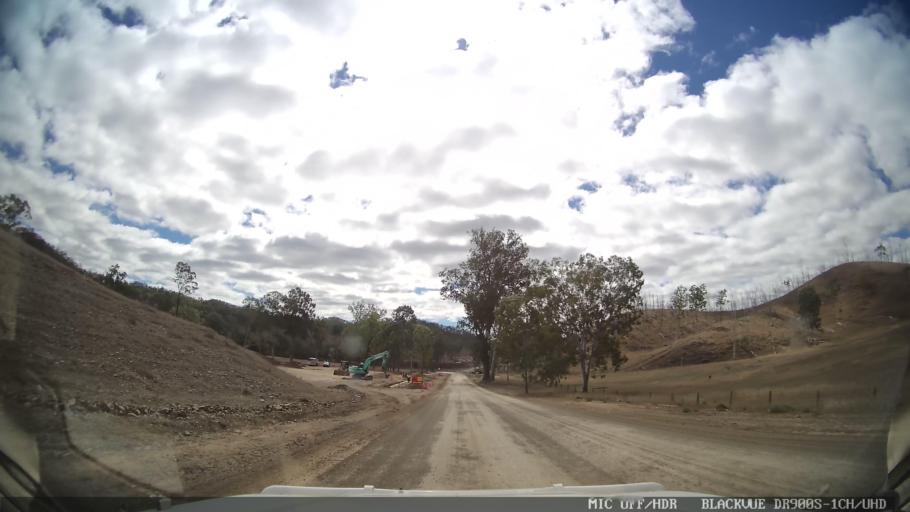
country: AU
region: Queensland
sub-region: Gladstone
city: Toolooa
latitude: -24.6172
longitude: 151.2985
